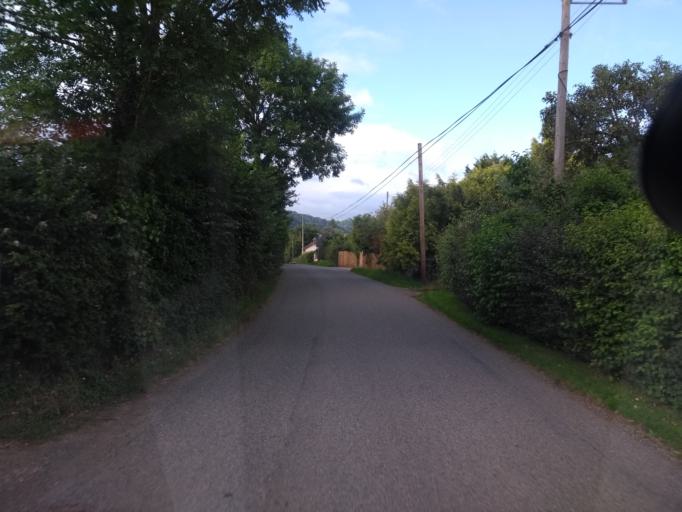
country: GB
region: England
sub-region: Somerset
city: Creech Saint Michael
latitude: 51.0128
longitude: -2.9774
